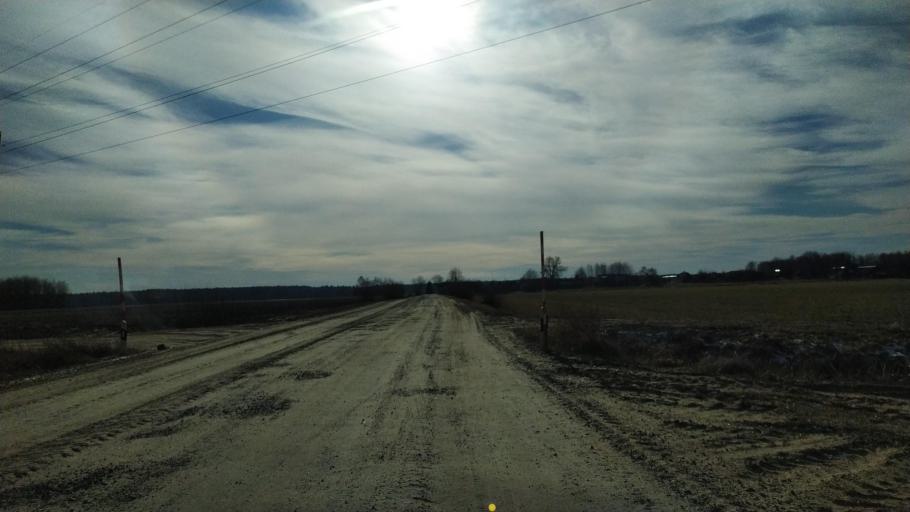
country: BY
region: Brest
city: Pruzhany
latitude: 52.5541
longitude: 24.2958
